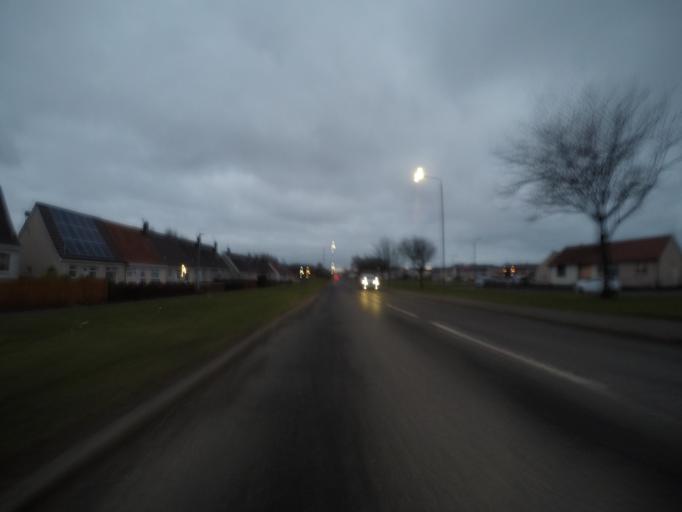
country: GB
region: Scotland
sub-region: North Ayrshire
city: Kilwinning
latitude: 55.6506
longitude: -4.6991
